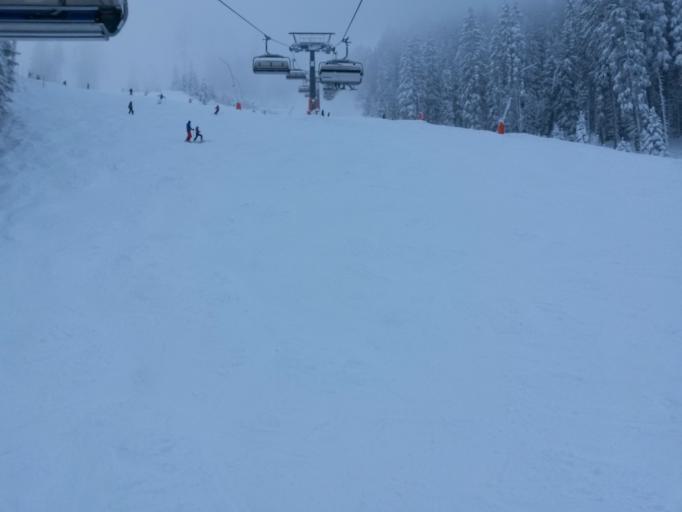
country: AT
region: Salzburg
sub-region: Politischer Bezirk Sankt Johann im Pongau
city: Dorfgastein
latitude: 47.2381
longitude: 13.1773
